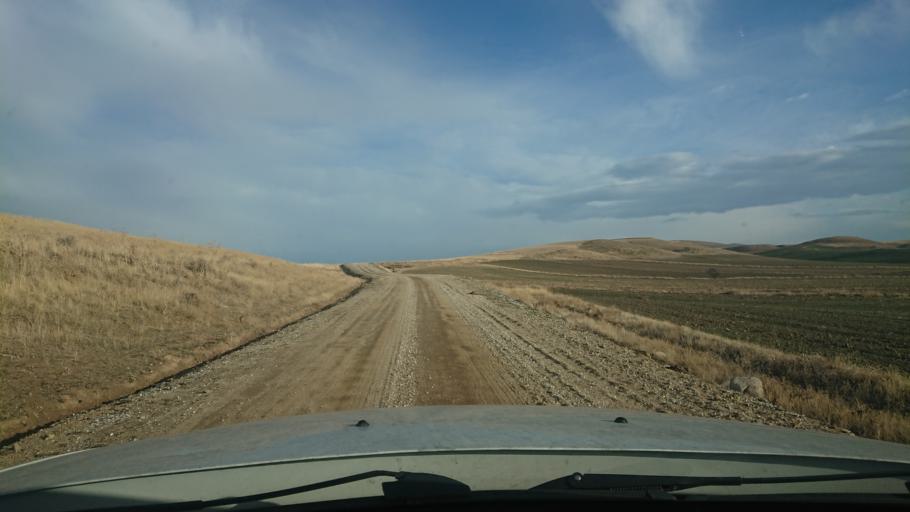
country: TR
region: Aksaray
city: Acipinar
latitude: 38.6868
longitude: 33.8696
